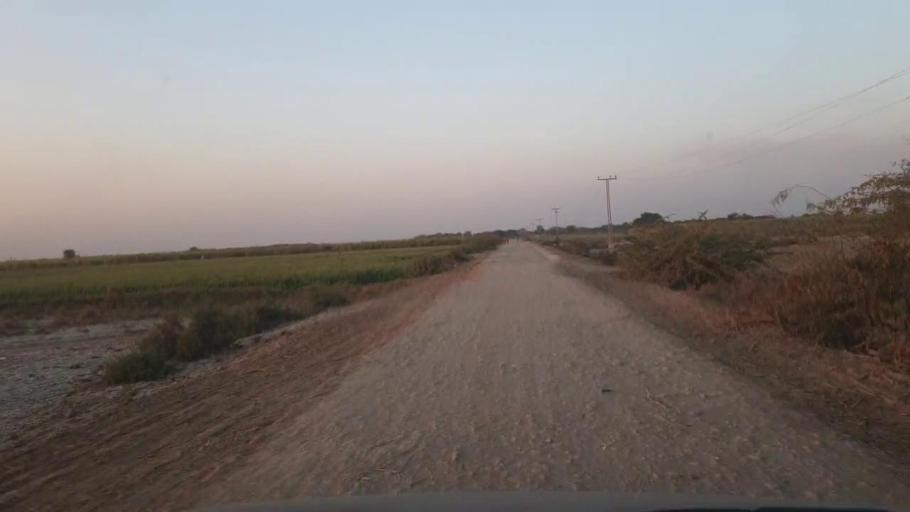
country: PK
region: Sindh
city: Chambar
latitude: 25.3052
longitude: 68.9075
